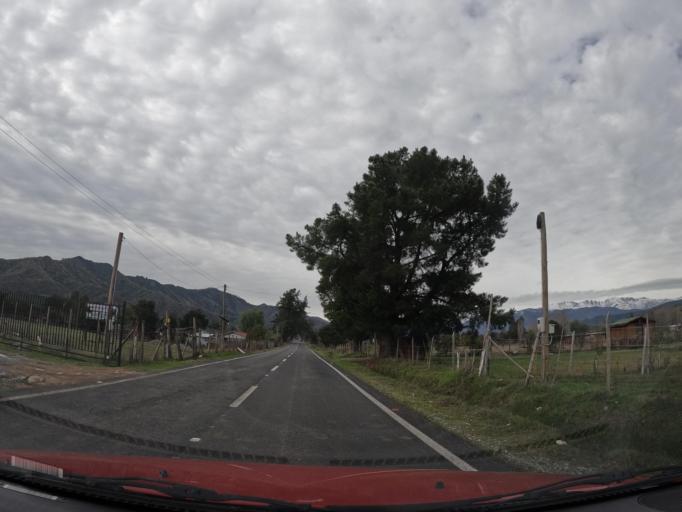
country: CL
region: Maule
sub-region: Provincia de Linares
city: Linares
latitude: -35.9266
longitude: -71.4214
